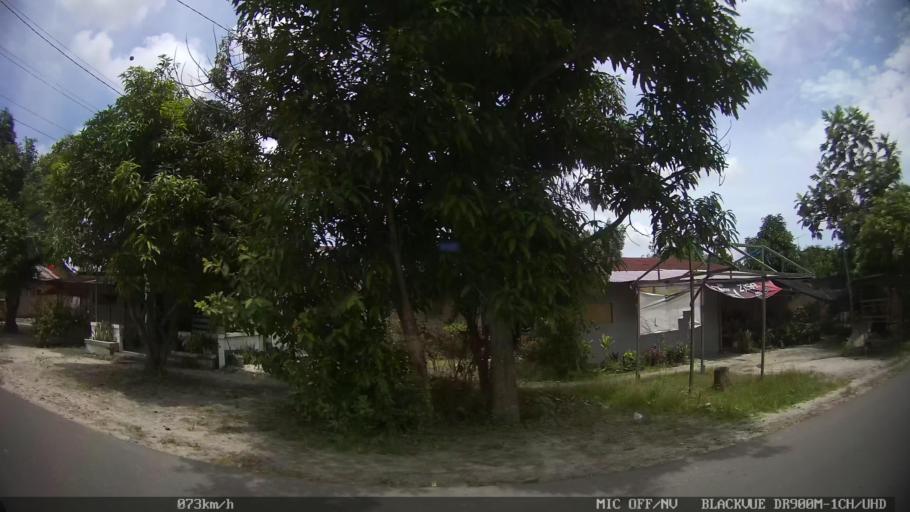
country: ID
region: North Sumatra
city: Percut
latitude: 3.5848
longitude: 98.8833
